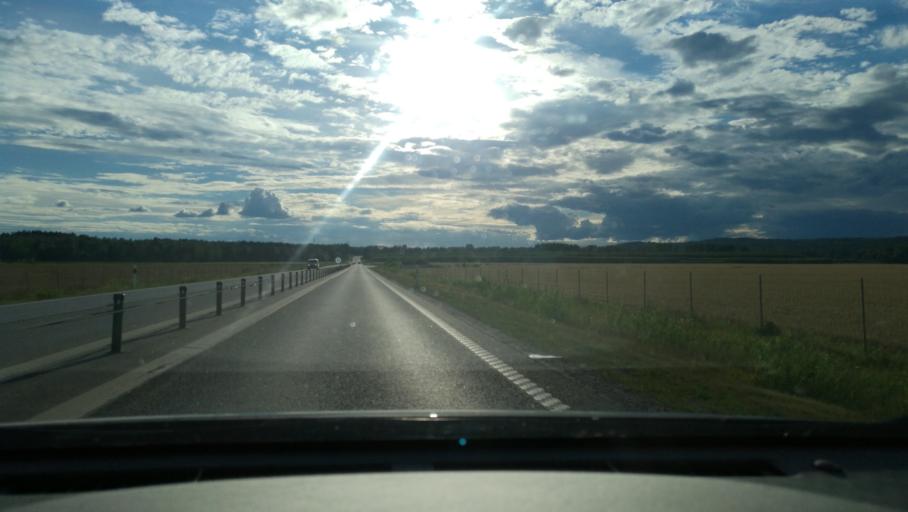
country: SE
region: OEstergoetland
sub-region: Norrkopings Kommun
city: Jursla
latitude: 58.6330
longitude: 16.1320
